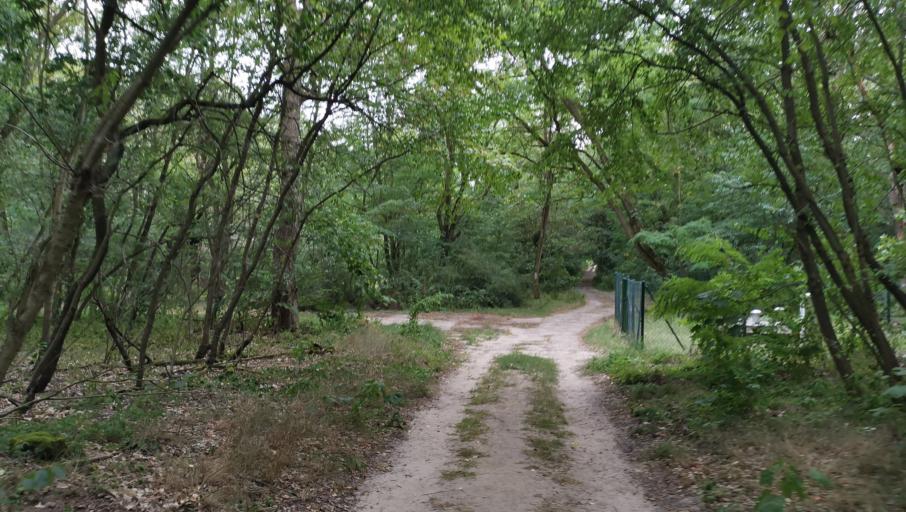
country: DE
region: Brandenburg
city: Potsdam
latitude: 52.3784
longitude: 13.0430
